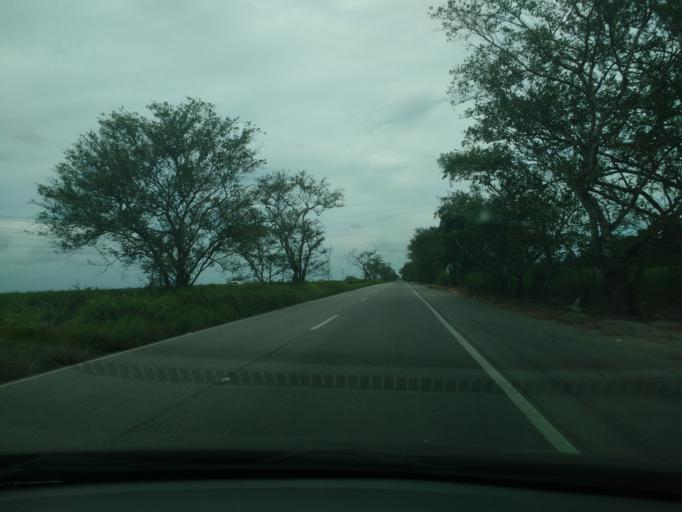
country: BR
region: Alagoas
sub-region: Rio Largo
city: Rio Largo
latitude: -9.4498
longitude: -35.8321
